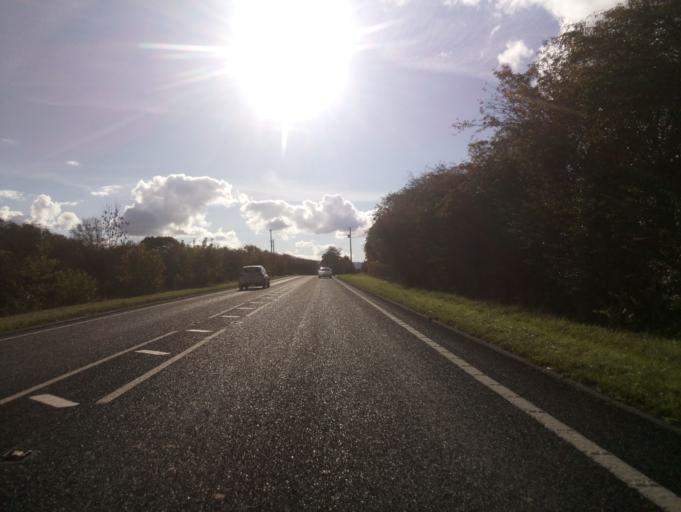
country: GB
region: Wales
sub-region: Sir Powys
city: Brecon
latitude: 51.9731
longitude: -3.3361
